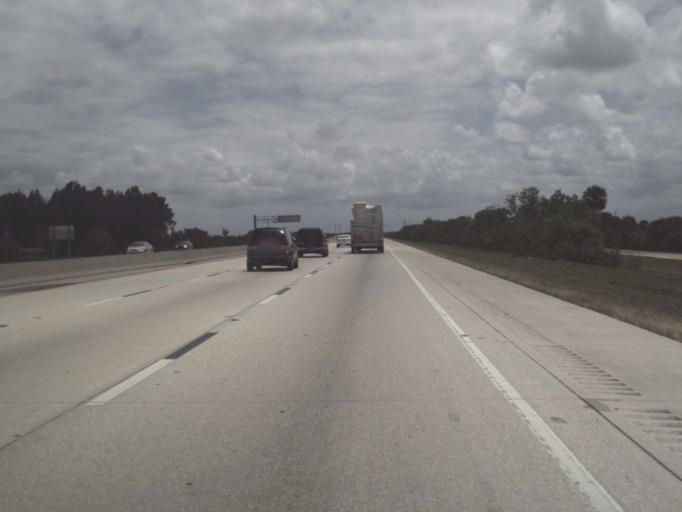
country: US
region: Florida
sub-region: Brevard County
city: Cocoa West
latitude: 28.3416
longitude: -80.7828
